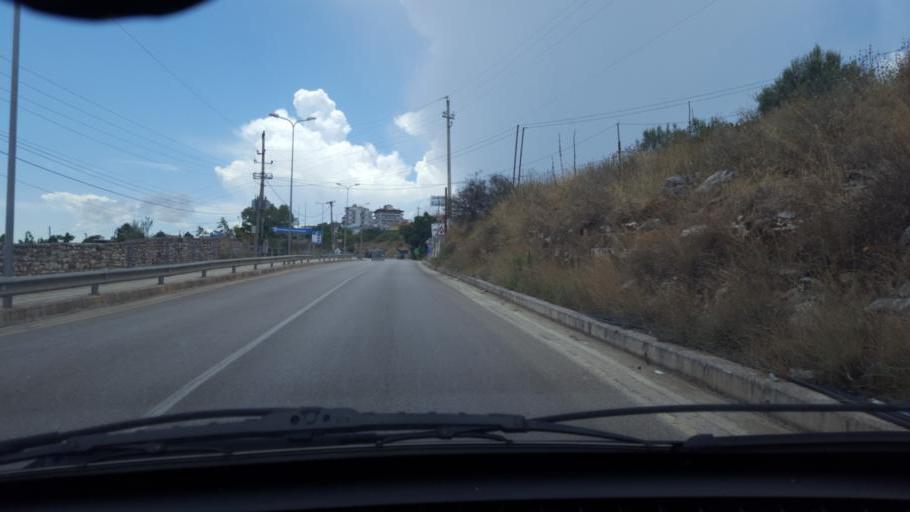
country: AL
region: Vlore
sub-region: Rrethi i Sarandes
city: Sarande
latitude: 39.8461
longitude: 20.0247
